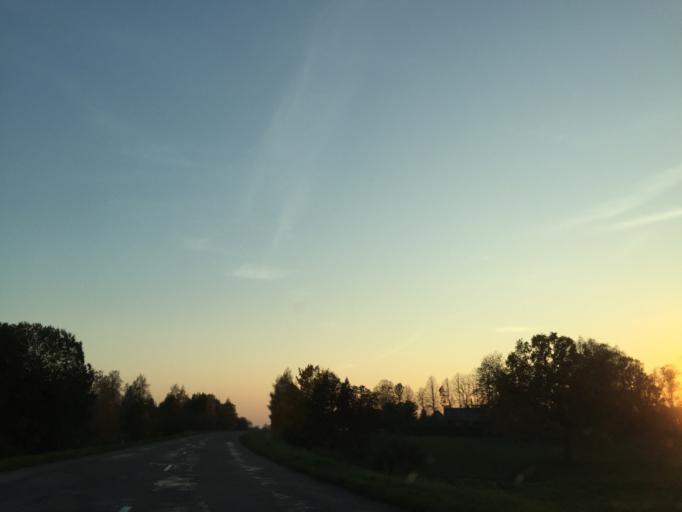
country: LT
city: Skuodas
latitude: 56.3101
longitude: 21.5485
